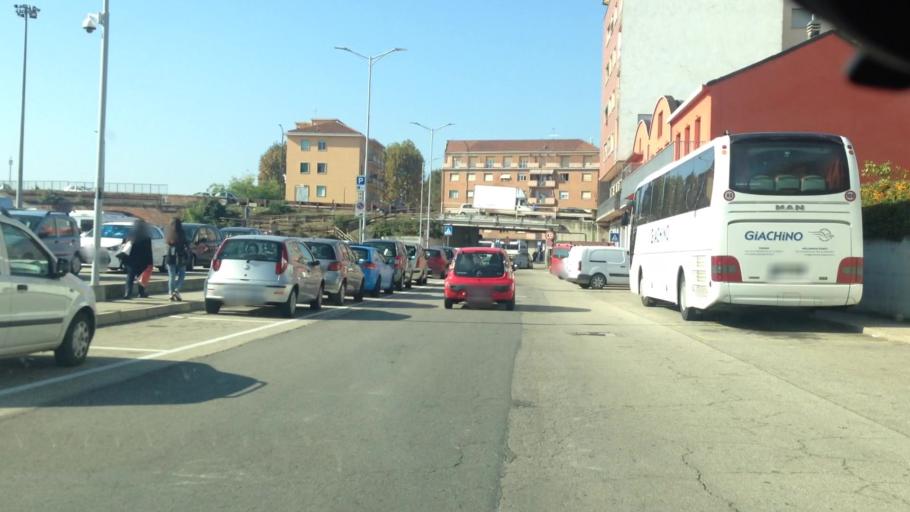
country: IT
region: Piedmont
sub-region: Provincia di Asti
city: Asti
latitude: 44.8964
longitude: 8.2108
